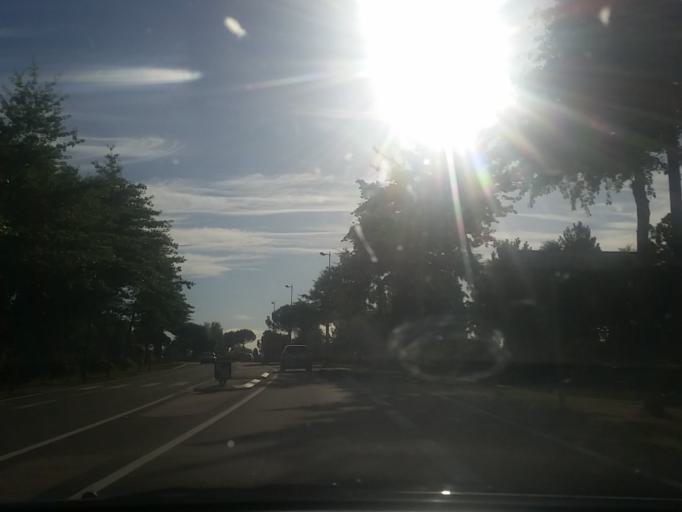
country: FR
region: Pays de la Loire
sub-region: Departement de la Loire-Atlantique
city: Bouguenais
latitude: 47.1769
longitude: -1.6181
